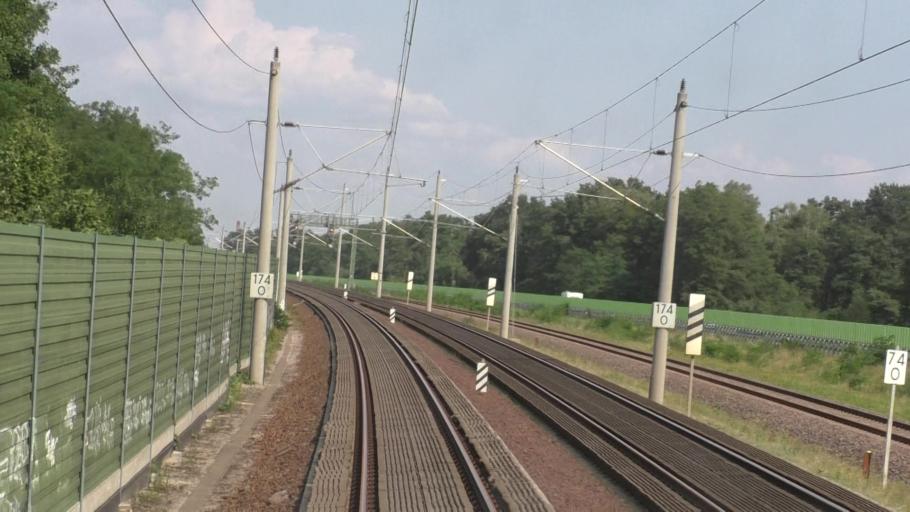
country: DE
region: Brandenburg
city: Rathenow
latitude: 52.5913
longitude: 12.3100
